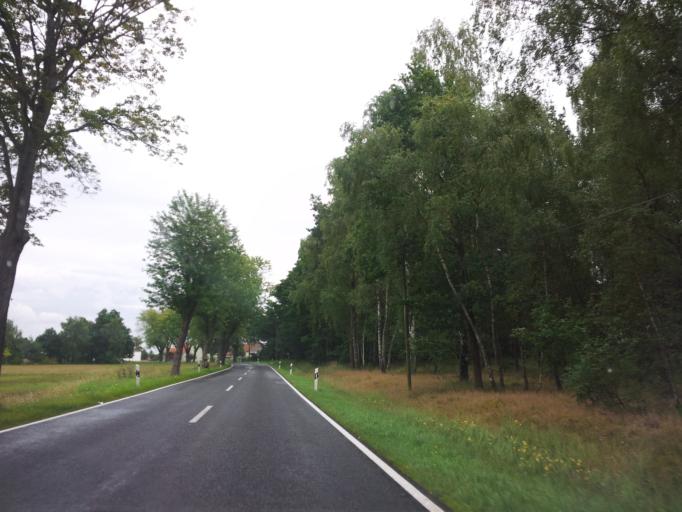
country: DE
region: Brandenburg
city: Wiesenburg
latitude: 52.1666
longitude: 12.4581
